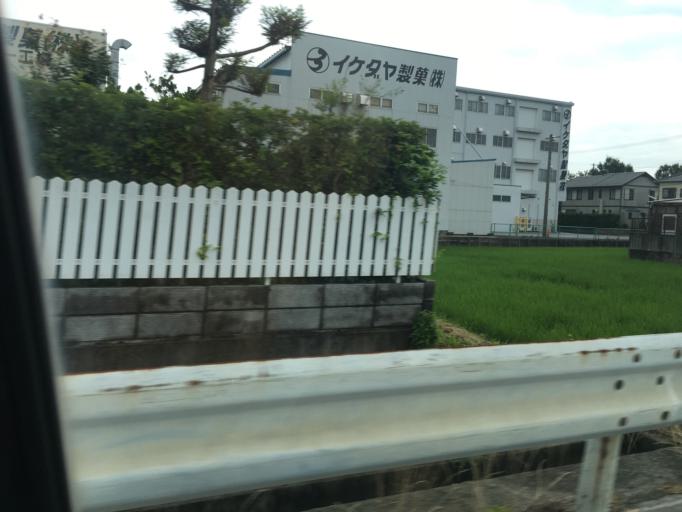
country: JP
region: Aichi
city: Ishiki
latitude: 34.8045
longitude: 137.0190
